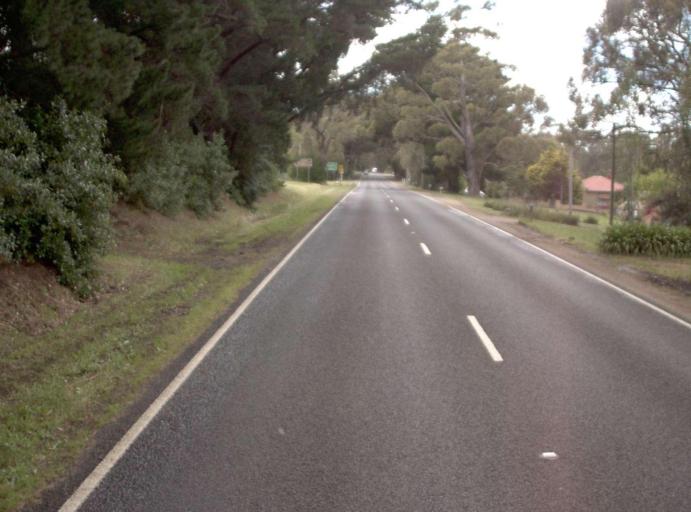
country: AU
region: Victoria
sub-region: Mornington Peninsula
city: Dromana
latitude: -38.3642
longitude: 144.9912
